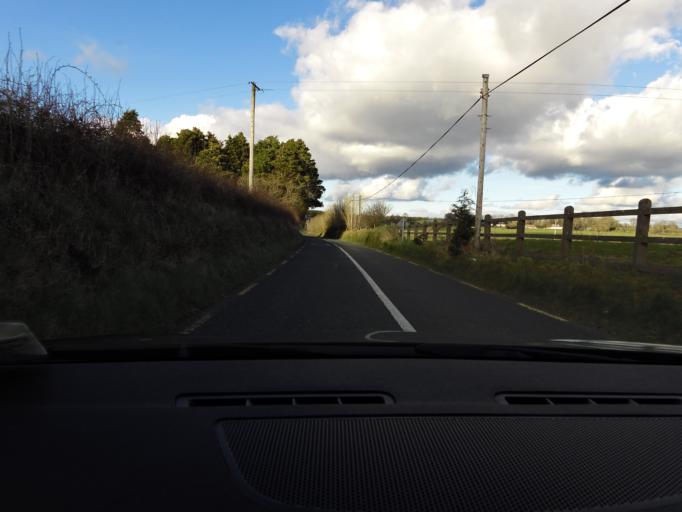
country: IE
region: Connaught
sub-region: Roscommon
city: Castlerea
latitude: 53.6493
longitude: -8.5198
